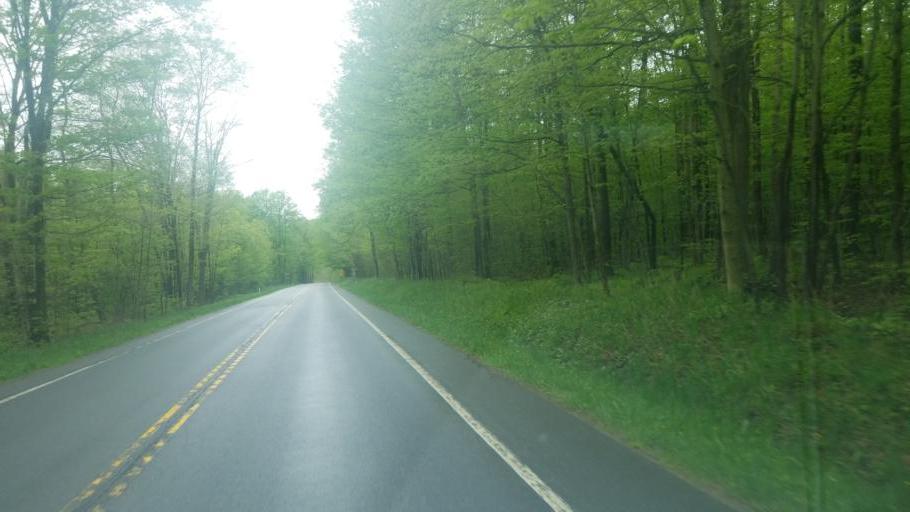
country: US
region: Pennsylvania
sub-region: McKean County
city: Kane
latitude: 41.6052
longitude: -78.8418
